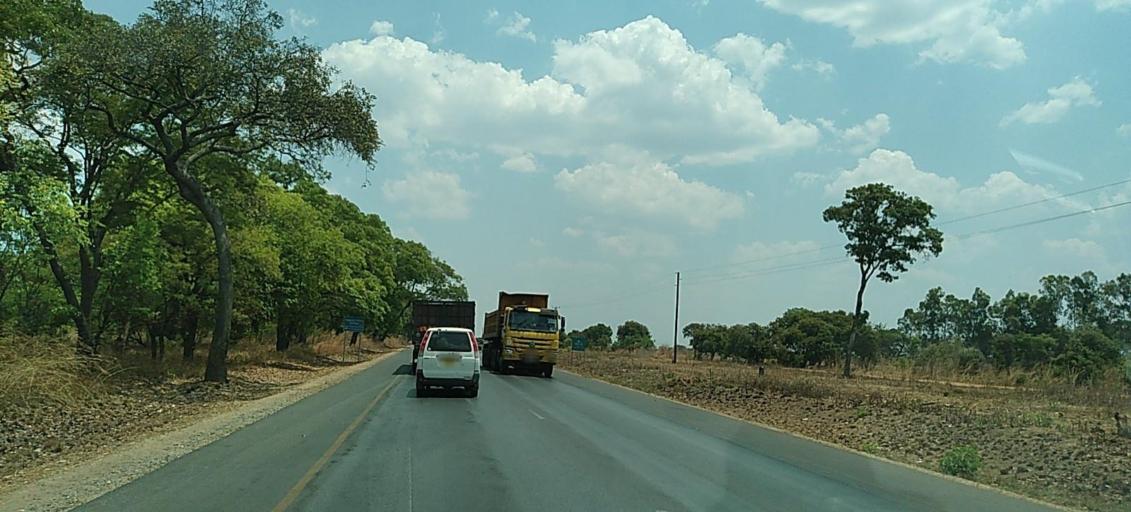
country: ZM
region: Central
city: Kabwe
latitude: -14.2315
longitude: 28.5718
